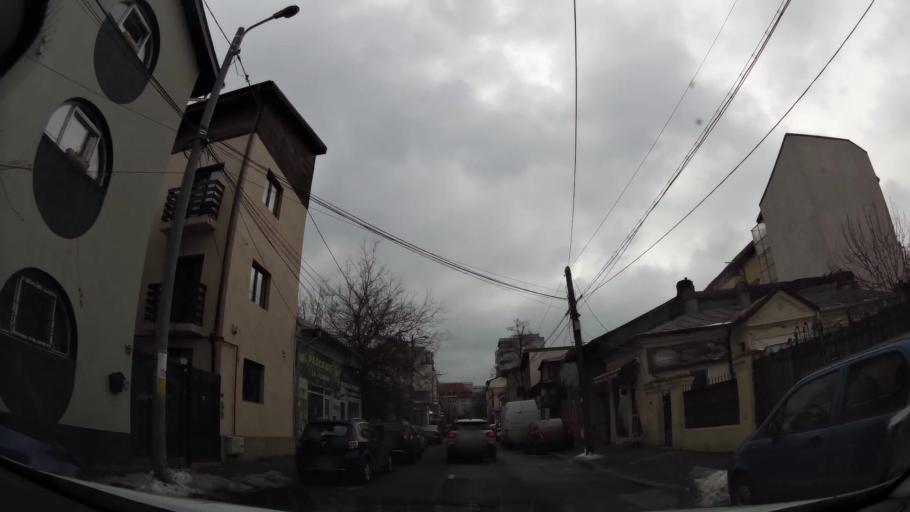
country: RO
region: Bucuresti
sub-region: Municipiul Bucuresti
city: Bucuresti
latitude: 44.4557
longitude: 26.0752
